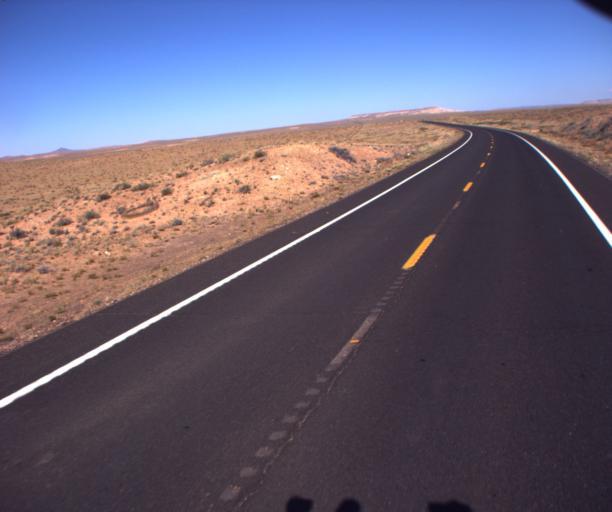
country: US
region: Arizona
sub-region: Coconino County
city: Tuba City
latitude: 36.1659
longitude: -111.0929
